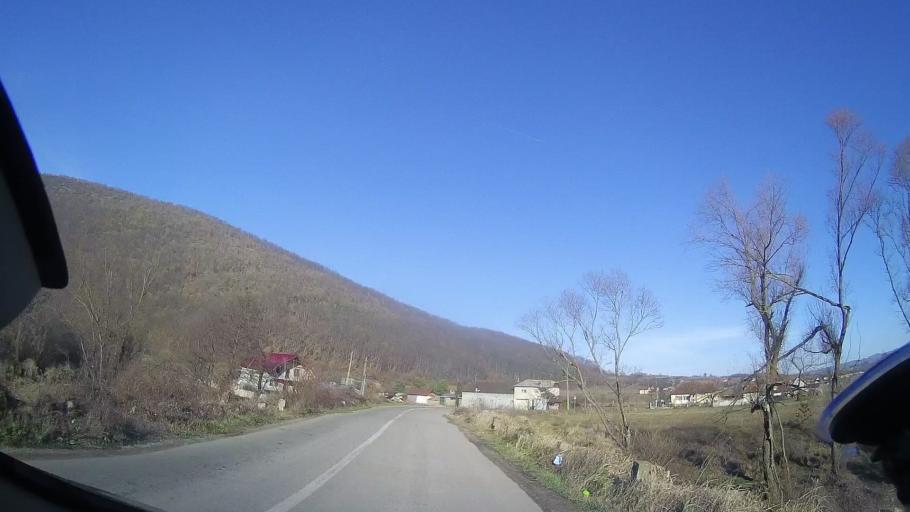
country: RO
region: Bihor
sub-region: Comuna Suncuius
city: Suncuius
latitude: 46.9515
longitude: 22.5307
